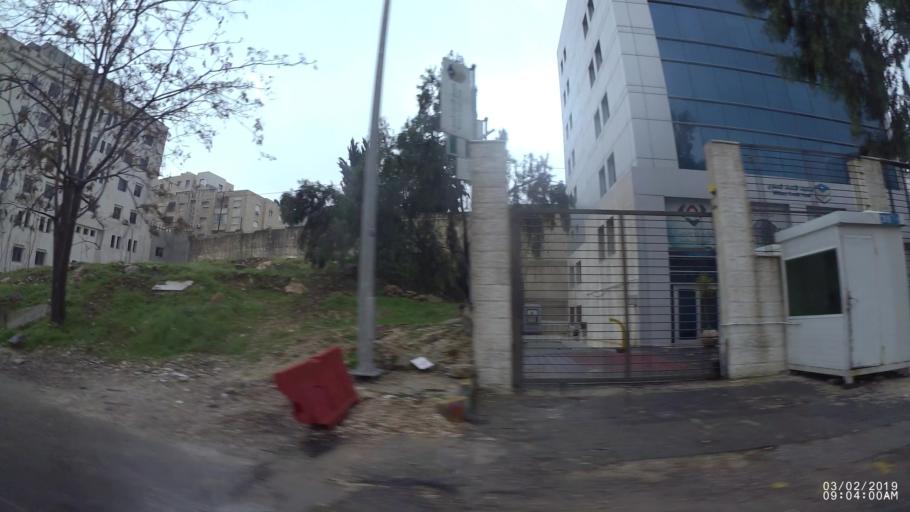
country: JO
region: Amman
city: Amman
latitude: 31.9591
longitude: 35.9026
